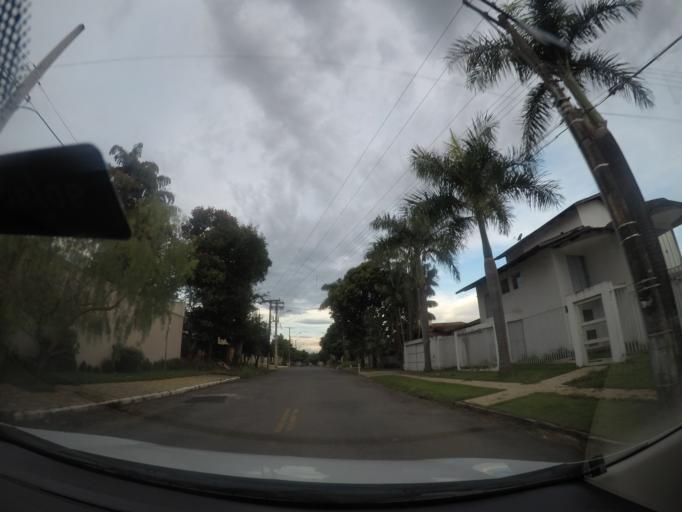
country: BR
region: Goias
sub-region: Goiania
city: Goiania
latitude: -16.6524
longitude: -49.2256
